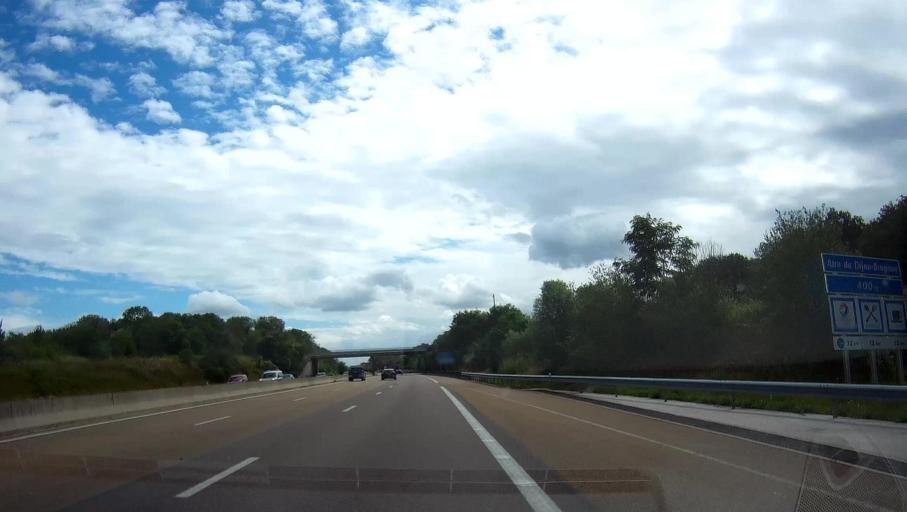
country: FR
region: Bourgogne
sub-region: Departement de la Cote-d'Or
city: Saint-Julien
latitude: 47.4317
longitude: 5.1677
